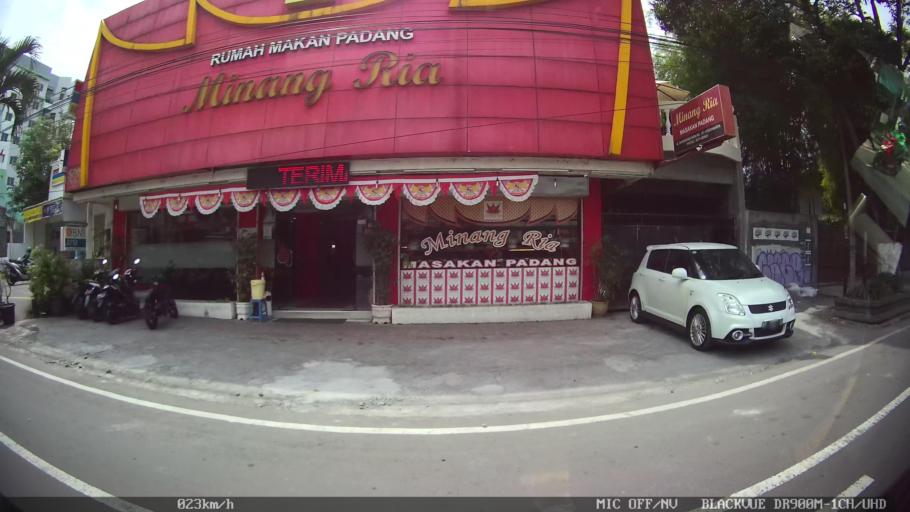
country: ID
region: Daerah Istimewa Yogyakarta
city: Yogyakarta
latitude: -7.8020
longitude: 110.3898
